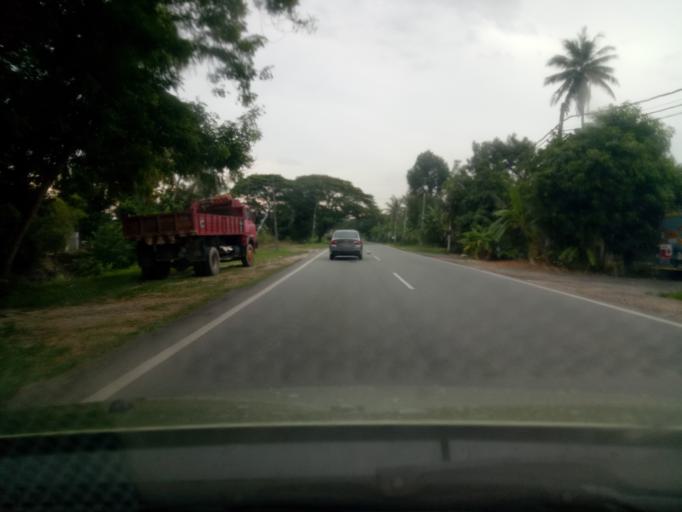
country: MY
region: Kedah
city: Gurun
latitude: 5.9694
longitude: 100.4323
